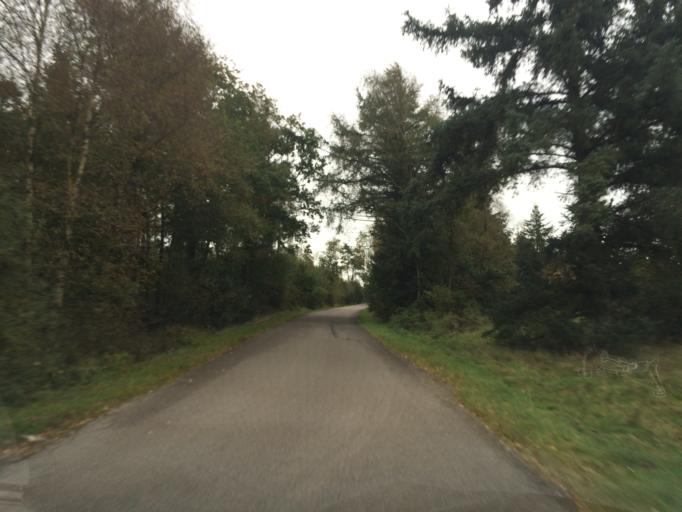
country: DK
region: Central Jutland
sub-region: Holstebro Kommune
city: Ulfborg
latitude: 56.2333
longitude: 8.4357
